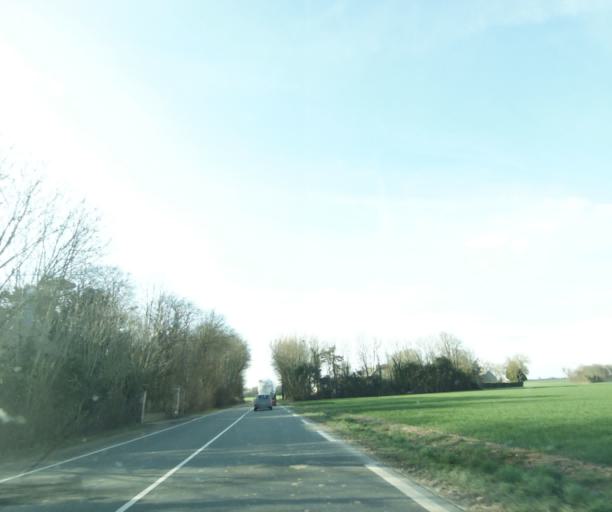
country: FR
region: Ile-de-France
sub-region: Departement des Yvelines
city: Ablis
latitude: 48.4699
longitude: 1.8677
